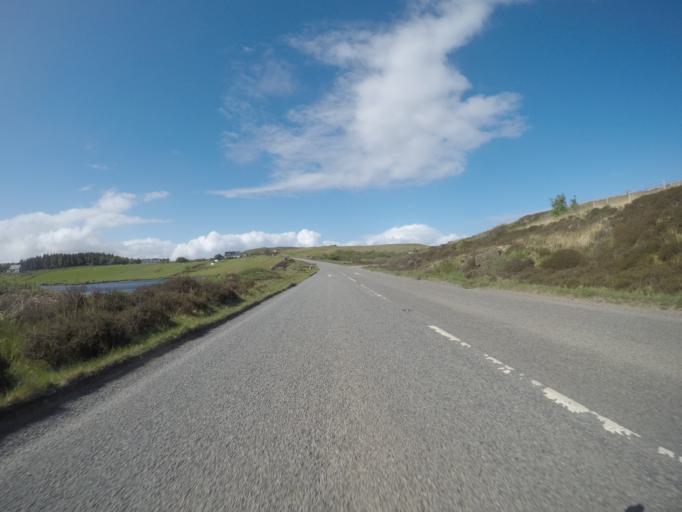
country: GB
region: Scotland
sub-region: Highland
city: Portree
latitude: 57.6090
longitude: -6.1745
